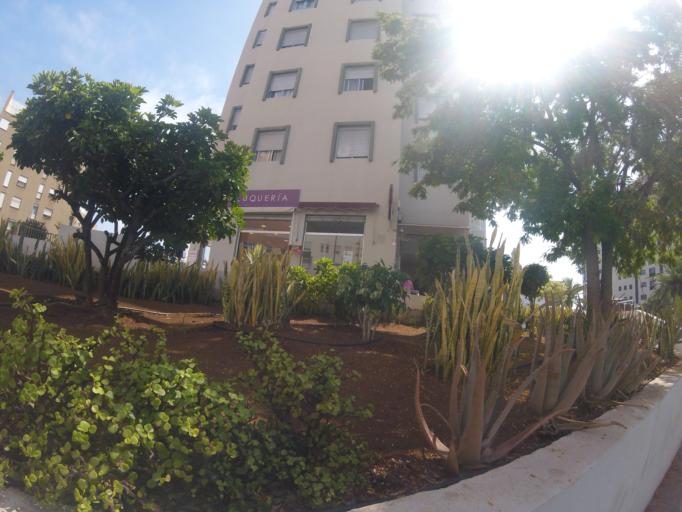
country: ES
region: Canary Islands
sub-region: Provincia de Santa Cruz de Tenerife
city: Santa Cruz de Tenerife
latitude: 28.4594
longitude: -16.2568
